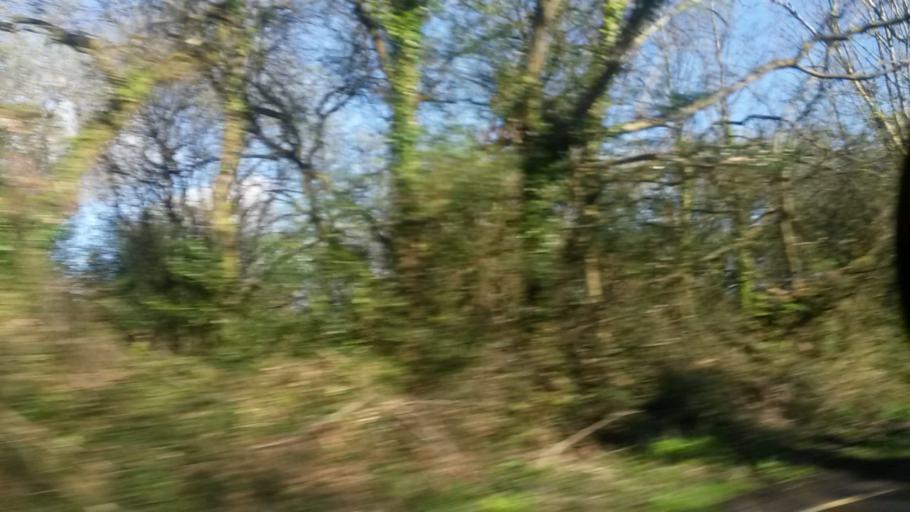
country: IE
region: Munster
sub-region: County Cork
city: Cobh
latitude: 51.8815
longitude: -8.3147
